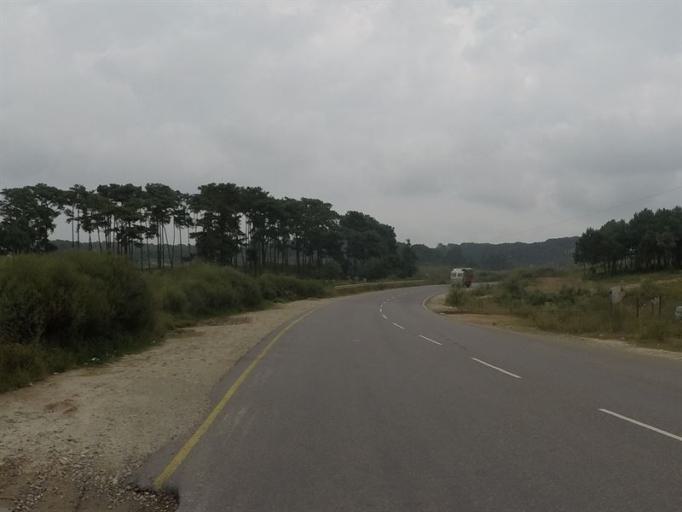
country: IN
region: Meghalaya
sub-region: East Khasi Hills
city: Shillong
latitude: 25.4952
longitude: 92.1729
